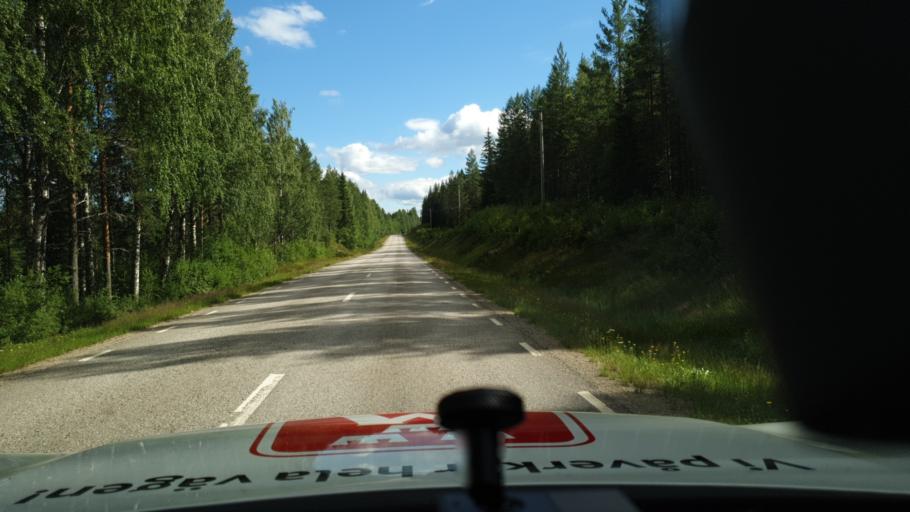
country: NO
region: Hedmark
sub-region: Trysil
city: Innbygda
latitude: 61.0131
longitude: 12.4773
